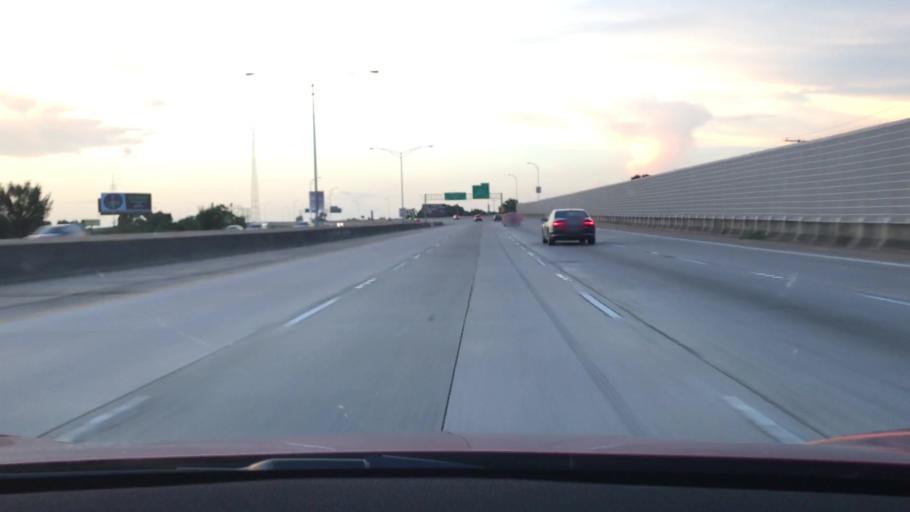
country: US
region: Louisiana
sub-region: Bossier Parish
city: Bossier City
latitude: 32.4873
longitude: -93.7549
